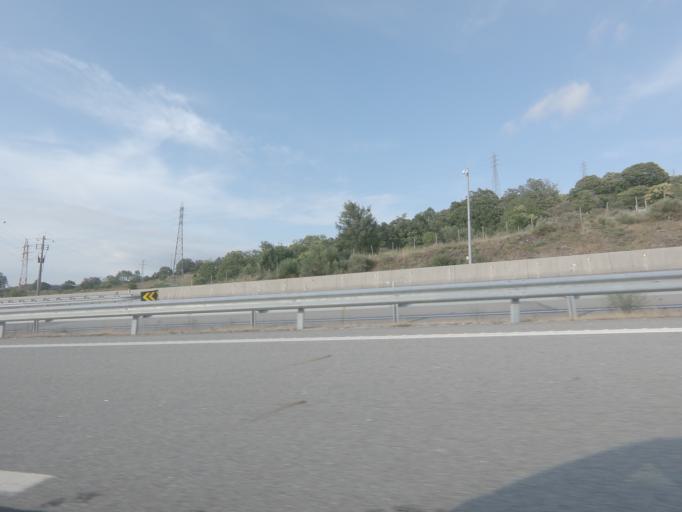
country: PT
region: Vila Real
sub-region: Vila Pouca de Aguiar
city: Vila Pouca de Aguiar
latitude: 41.4755
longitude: -7.6445
